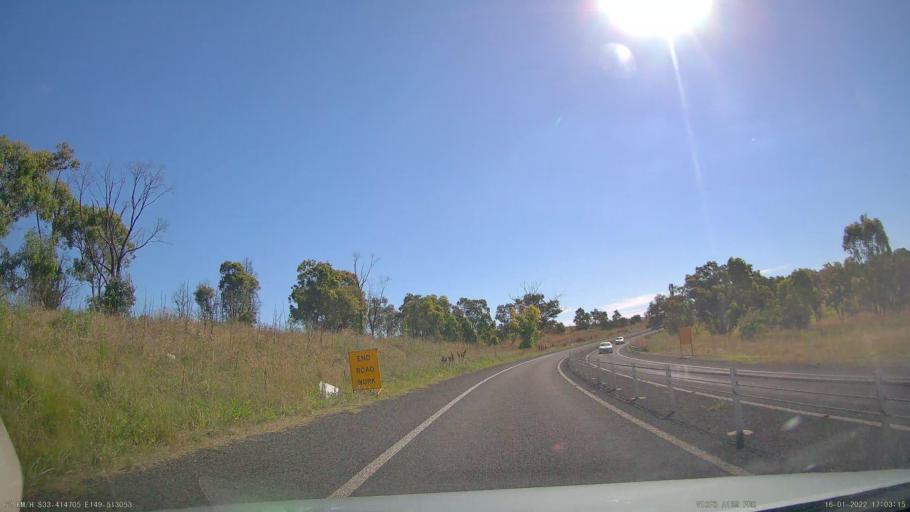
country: AU
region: New South Wales
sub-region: Bathurst Regional
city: Eglinton
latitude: -33.4148
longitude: 149.5129
